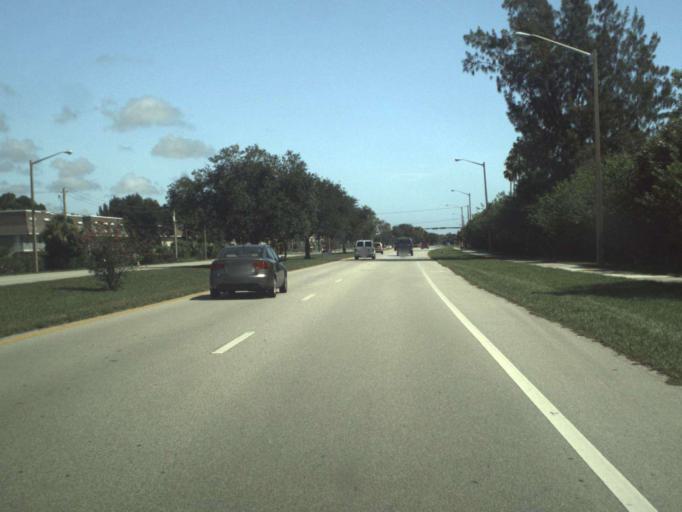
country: US
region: Florida
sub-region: Indian River County
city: Vero Beach
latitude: 27.6351
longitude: -80.3795
